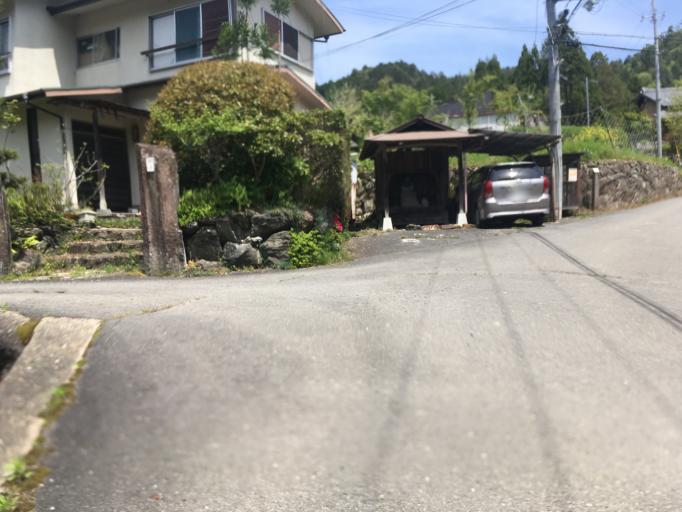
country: JP
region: Kyoto
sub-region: Kyoto-shi
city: Kamigyo-ku
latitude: 35.0844
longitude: 135.7219
